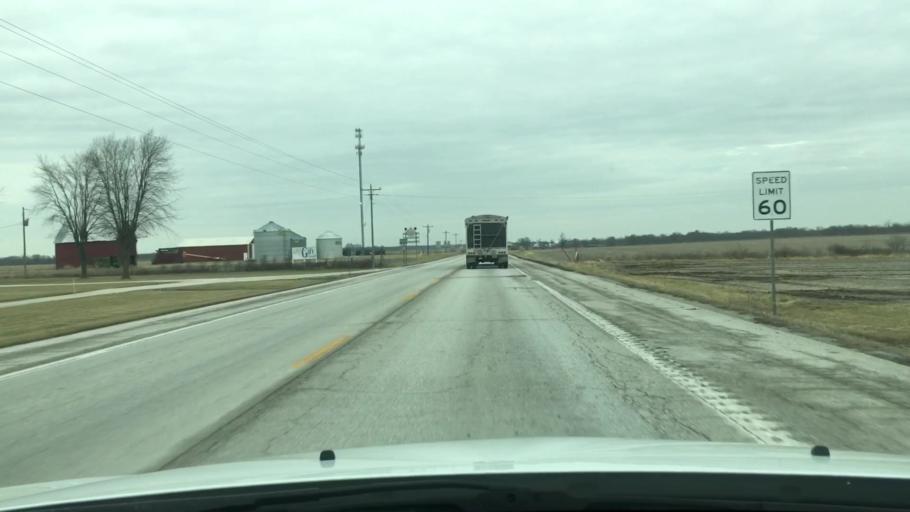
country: US
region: Missouri
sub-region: Montgomery County
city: Wellsville
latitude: 39.1656
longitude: -91.6479
